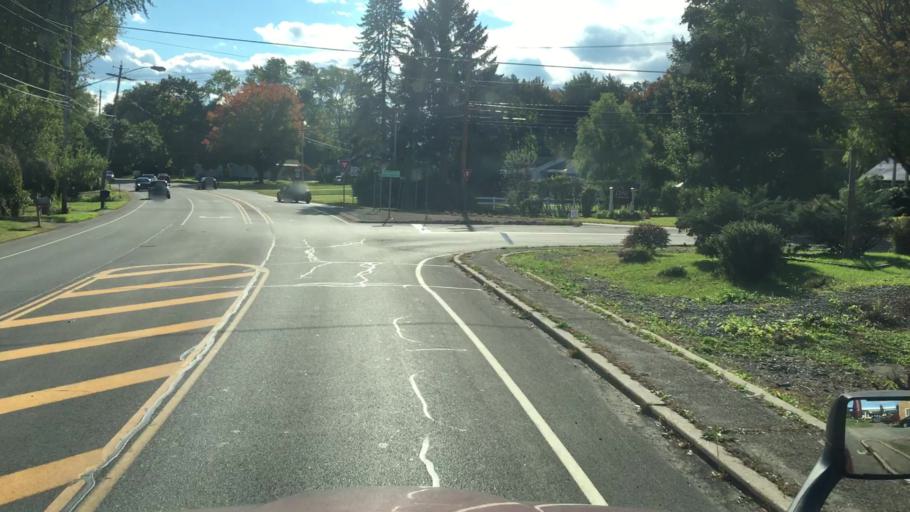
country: US
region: New York
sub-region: Schenectady County
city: Scotia
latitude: 42.8436
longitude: -73.9481
